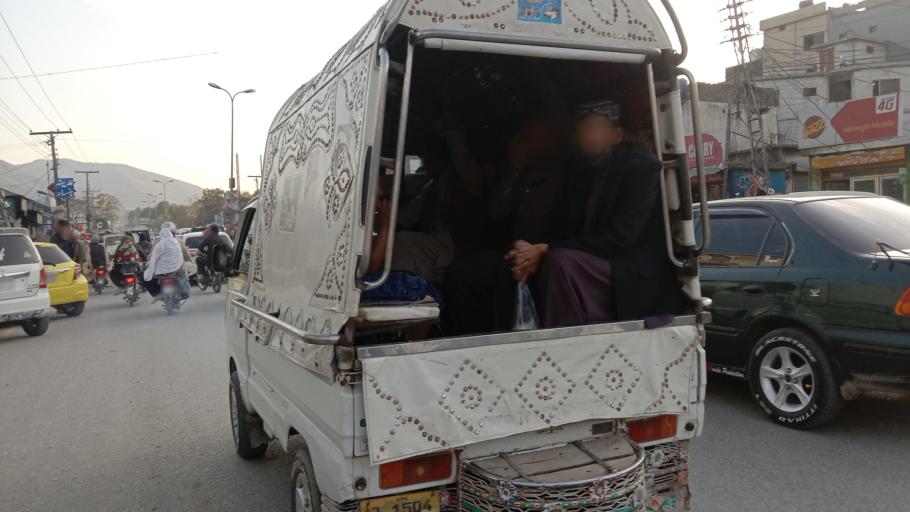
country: PK
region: Khyber Pakhtunkhwa
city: Abbottabad
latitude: 34.1687
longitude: 73.2248
